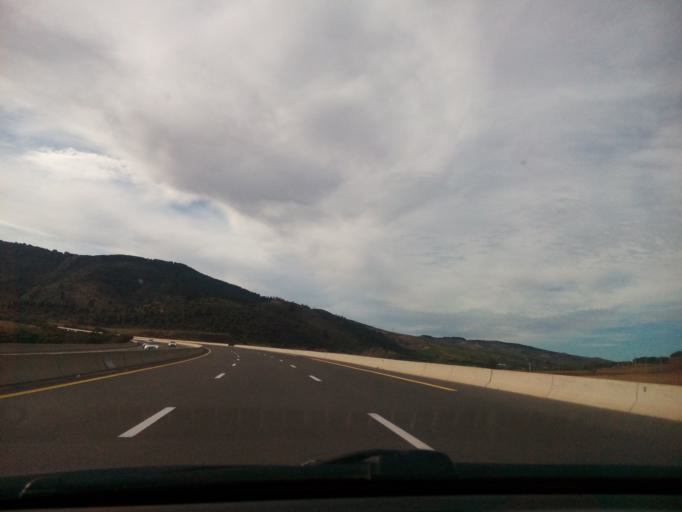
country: DZ
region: Sidi Bel Abbes
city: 'Ain el Berd
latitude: 35.4081
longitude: -0.4908
